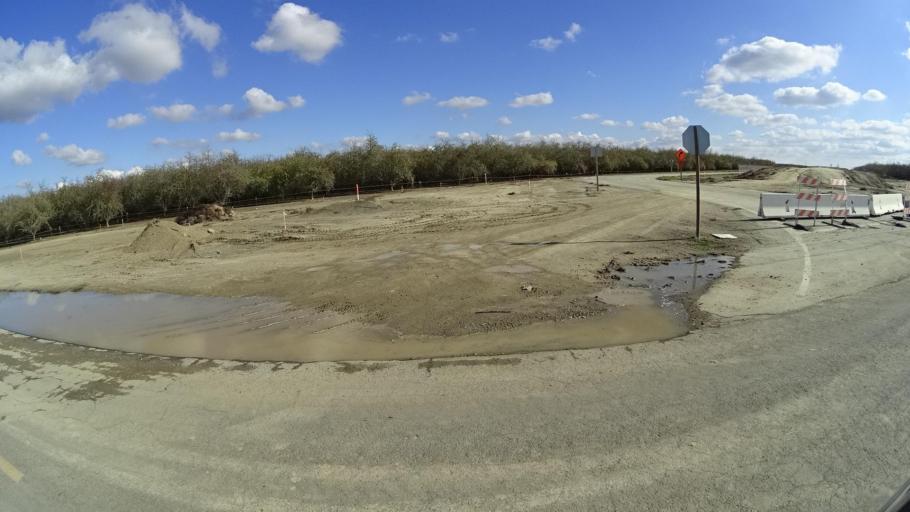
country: US
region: California
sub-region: Kern County
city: Delano
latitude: 35.7234
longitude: -119.3660
